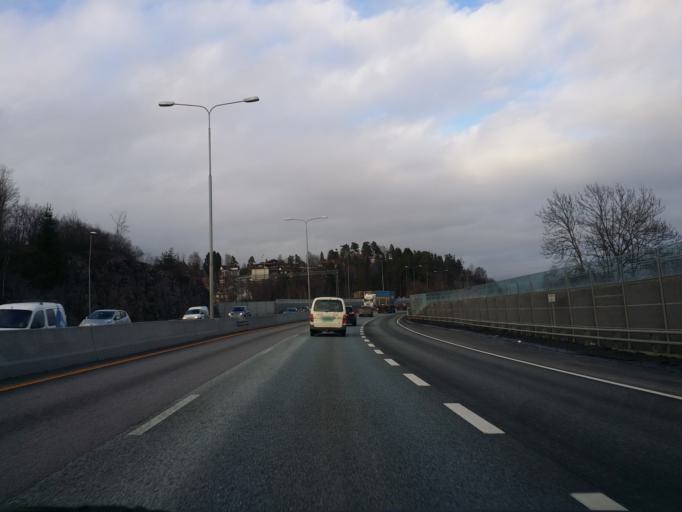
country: NO
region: Akershus
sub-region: Asker
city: Billingstad
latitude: 59.8770
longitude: 10.5044
